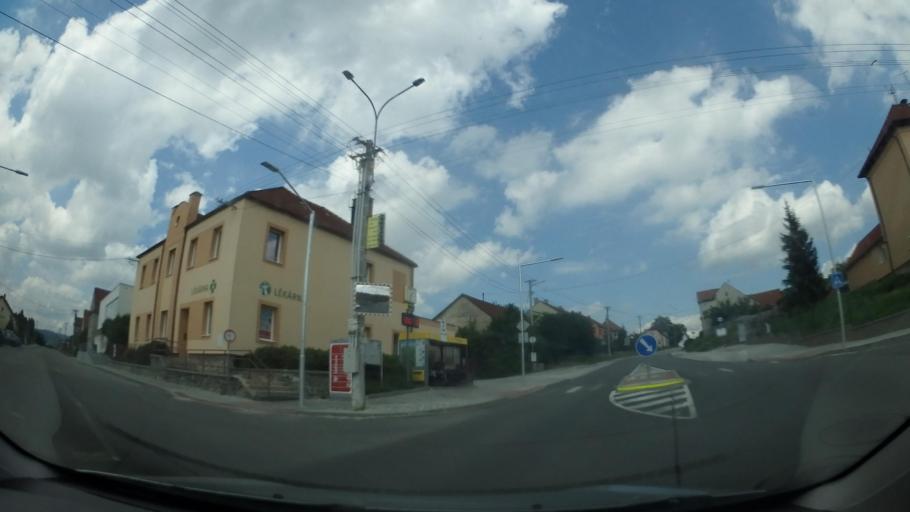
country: CZ
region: South Moravian
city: Velke Opatovice
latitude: 49.5492
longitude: 16.7097
